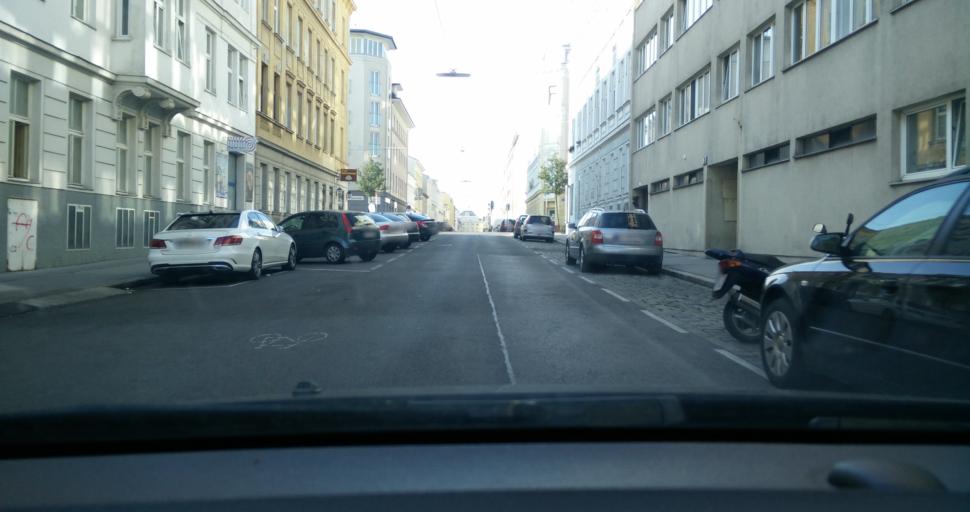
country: AT
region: Vienna
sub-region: Wien Stadt
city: Vienna
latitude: 48.2188
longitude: 16.3153
